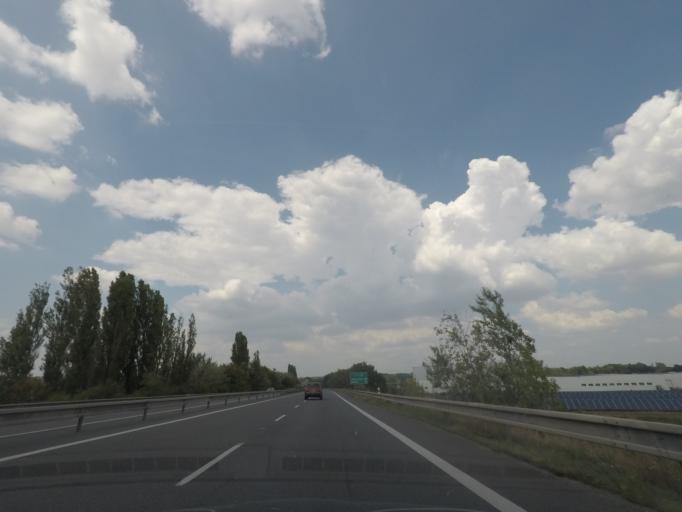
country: CZ
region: Olomoucky
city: Litovel
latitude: 49.6926
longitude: 17.0476
